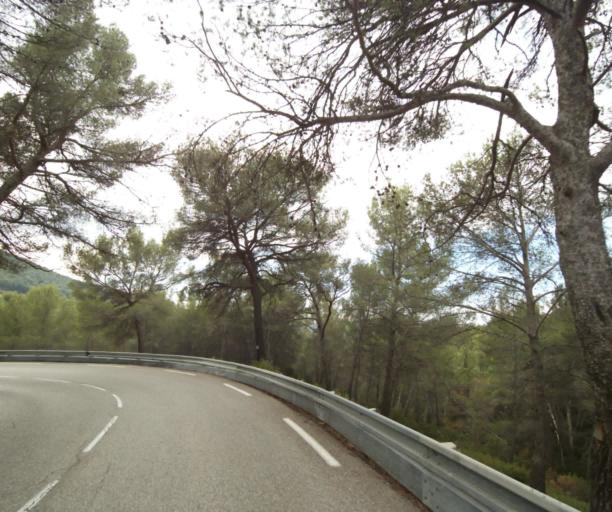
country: FR
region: Provence-Alpes-Cote d'Azur
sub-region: Departement des Bouches-du-Rhone
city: Ceyreste
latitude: 43.2267
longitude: 5.6478
